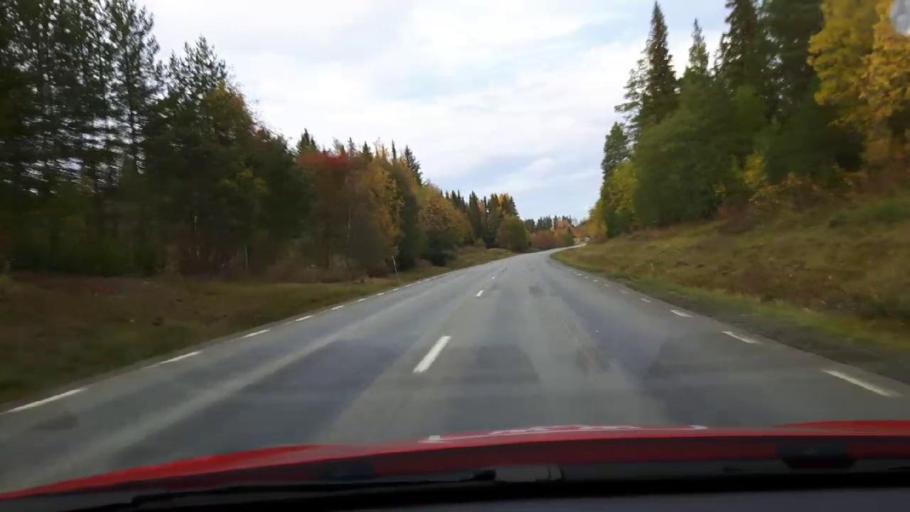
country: SE
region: Jaemtland
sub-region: Krokoms Kommun
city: Krokom
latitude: 63.3535
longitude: 14.4827
